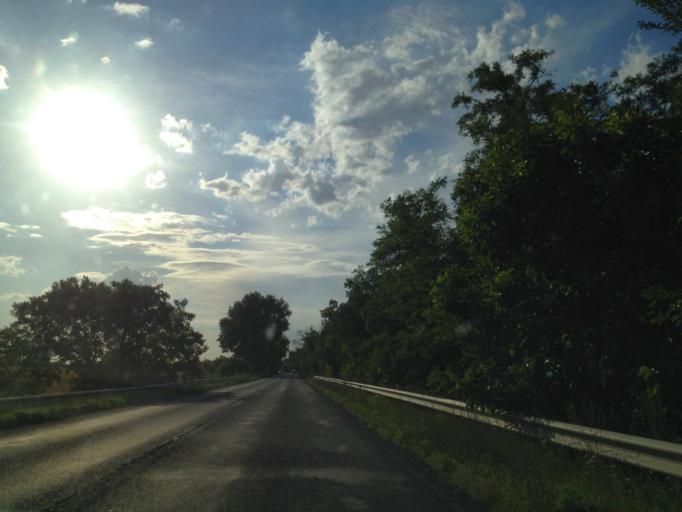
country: HU
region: Komarom-Esztergom
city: Acs
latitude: 47.7368
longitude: 17.9682
